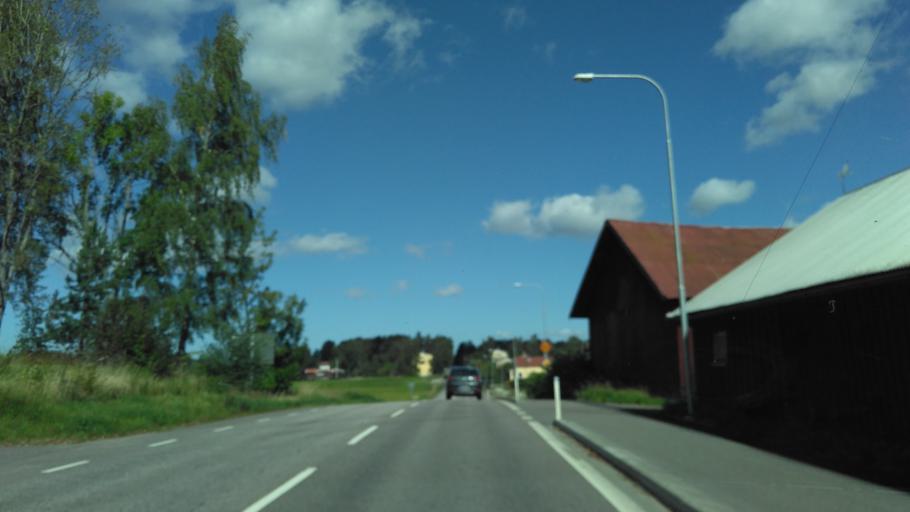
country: SE
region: Vaestra Goetaland
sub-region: Herrljunga Kommun
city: Herrljunga
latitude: 58.1723
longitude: 13.0011
